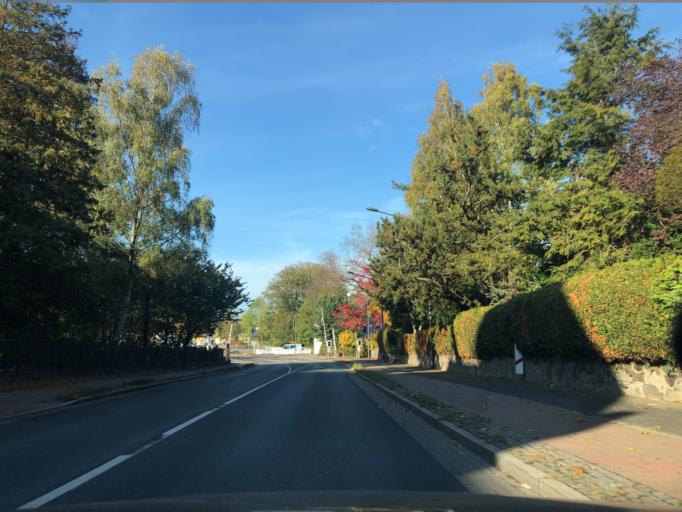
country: DE
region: Lower Saxony
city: Lemwerder
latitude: 53.1823
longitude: 8.5827
